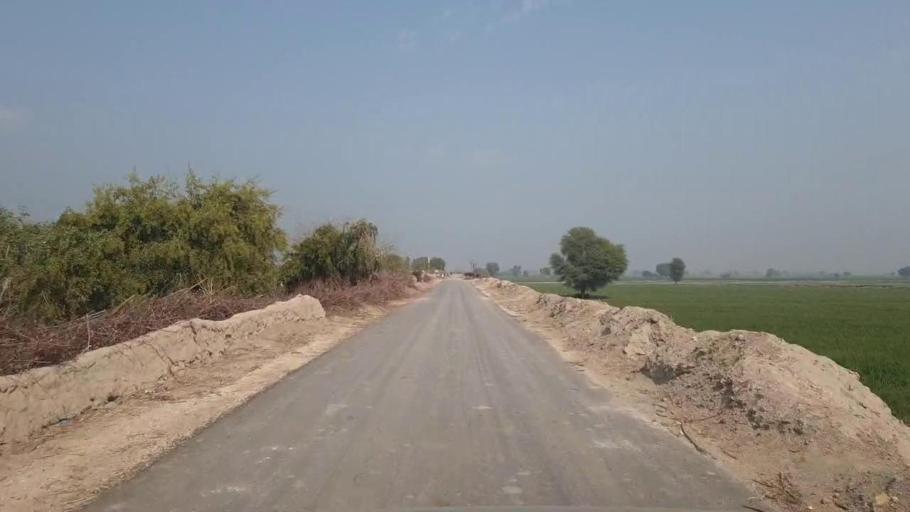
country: PK
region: Sindh
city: Hala
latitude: 25.7777
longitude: 68.3967
